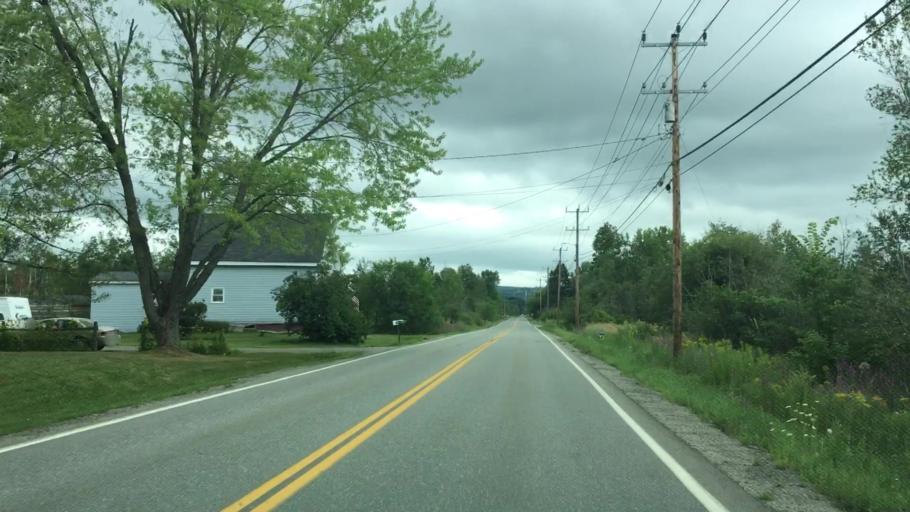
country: US
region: Maine
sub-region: Penobscot County
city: Brewer
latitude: 44.7670
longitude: -68.7550
